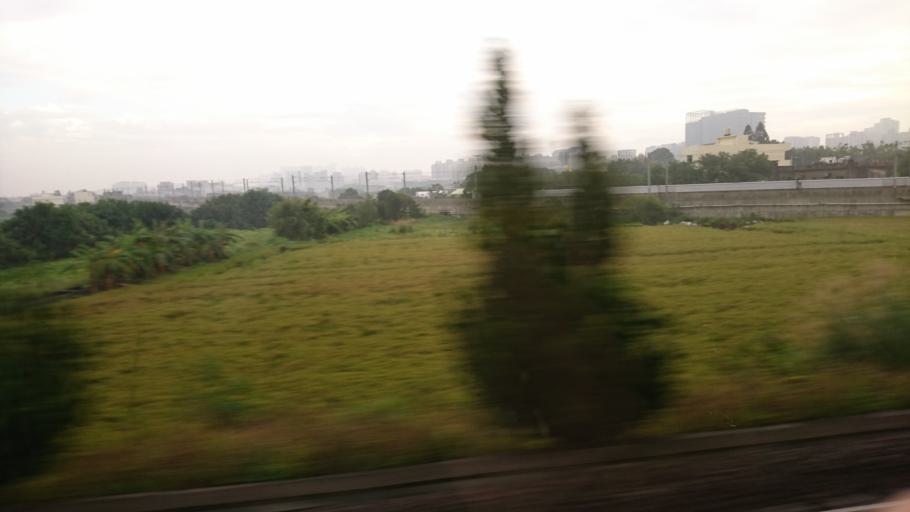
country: TW
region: Taiwan
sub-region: Hsinchu
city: Hsinchu
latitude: 24.8122
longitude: 120.9905
